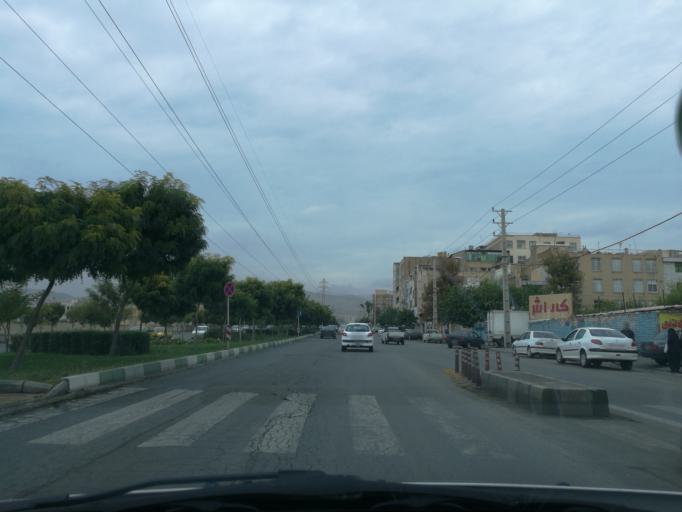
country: IR
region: Alborz
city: Karaj
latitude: 35.8522
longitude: 50.9189
